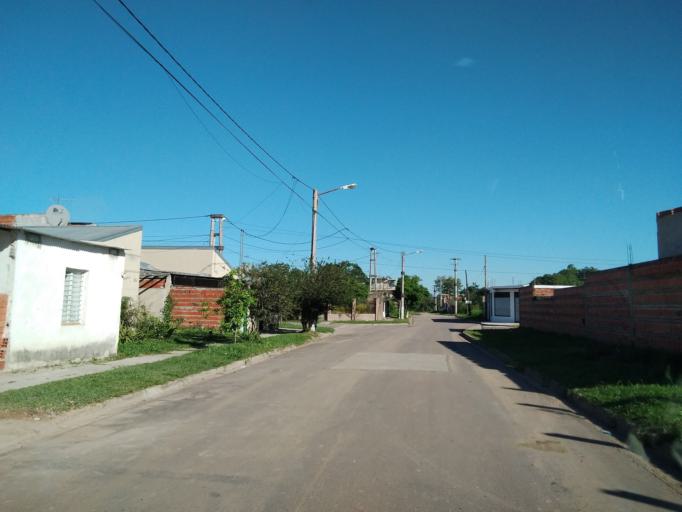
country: AR
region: Corrientes
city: Corrientes
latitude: -27.4580
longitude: -58.7700
